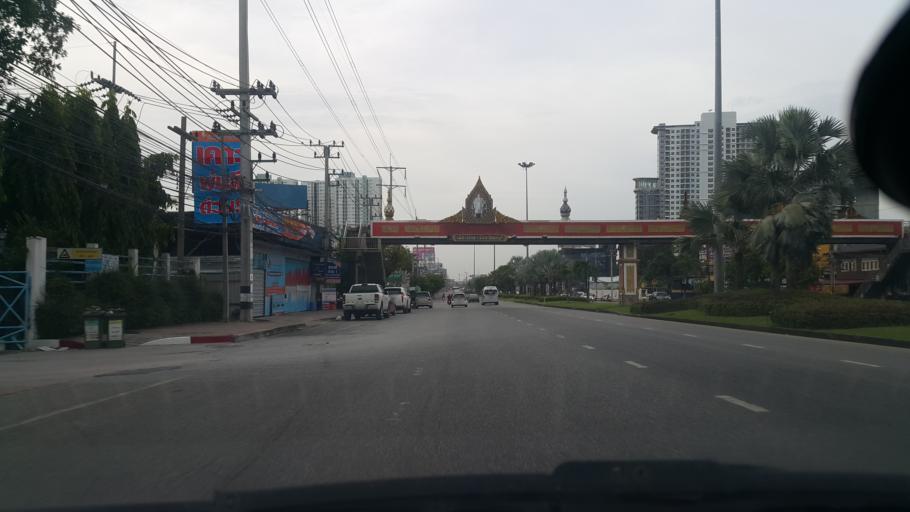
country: TH
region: Chon Buri
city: Phatthaya
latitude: 12.9589
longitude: 100.9083
